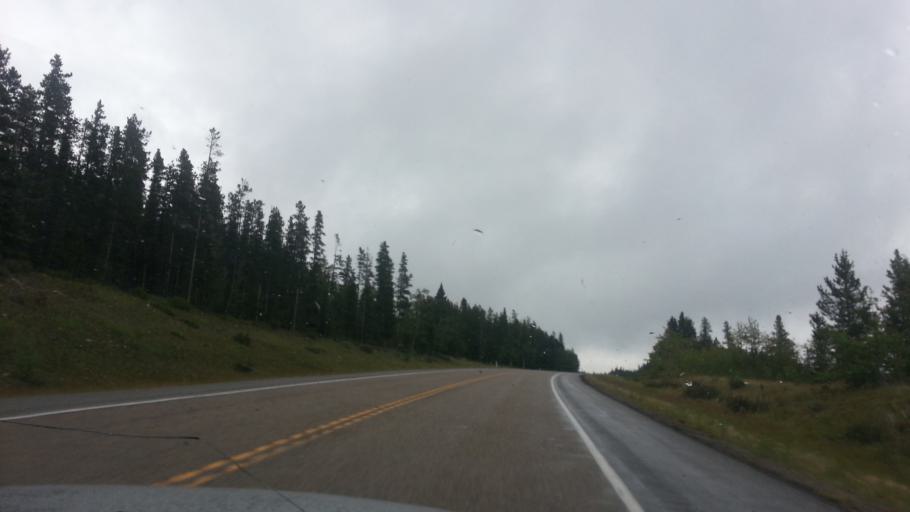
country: CA
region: Alberta
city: Cochrane
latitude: 50.8691
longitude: -114.7781
